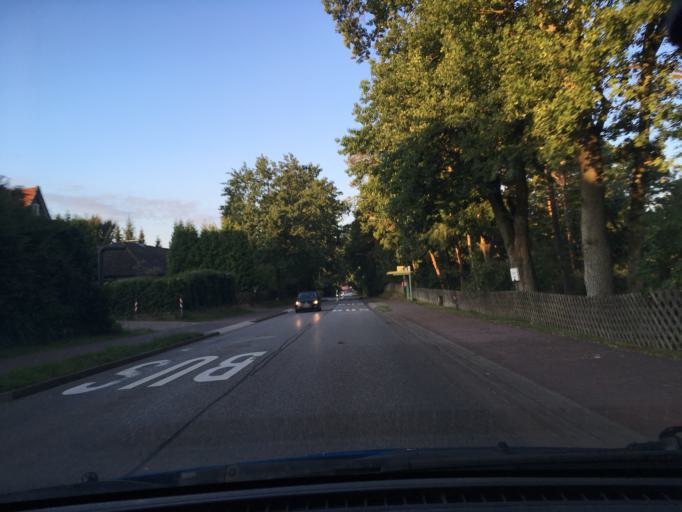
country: DE
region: Lower Saxony
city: Harmstorf
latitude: 53.3817
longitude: 10.0366
